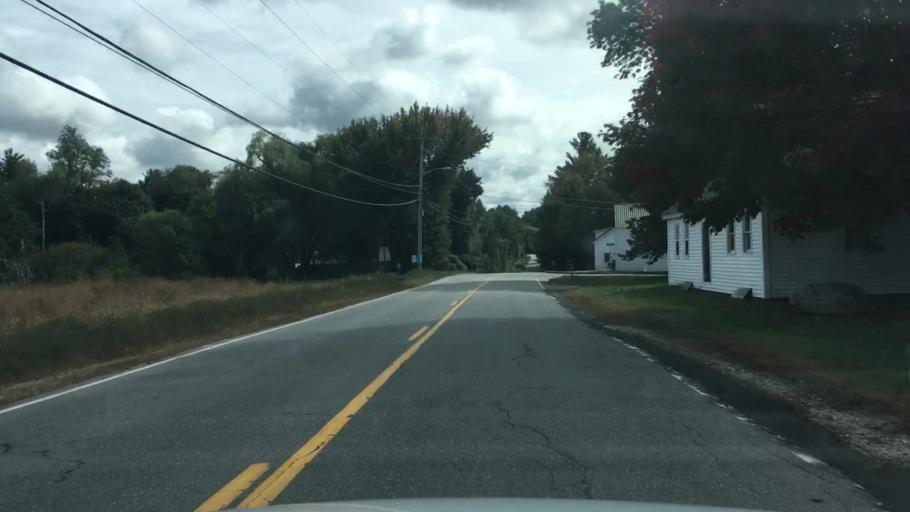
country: US
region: Maine
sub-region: Androscoggin County
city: Lewiston
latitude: 44.0519
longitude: -70.2008
